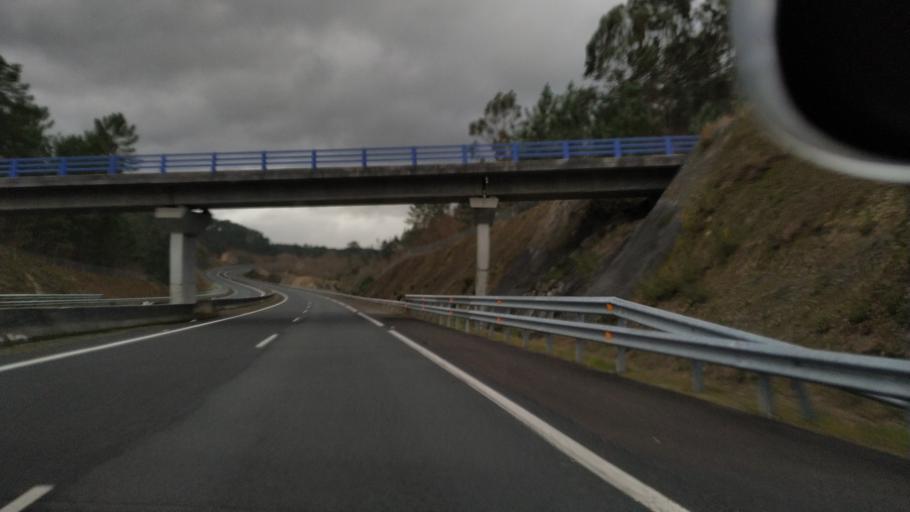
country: ES
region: Galicia
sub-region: Provincia da Coruna
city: Vedra
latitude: 42.7911
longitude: -8.4796
